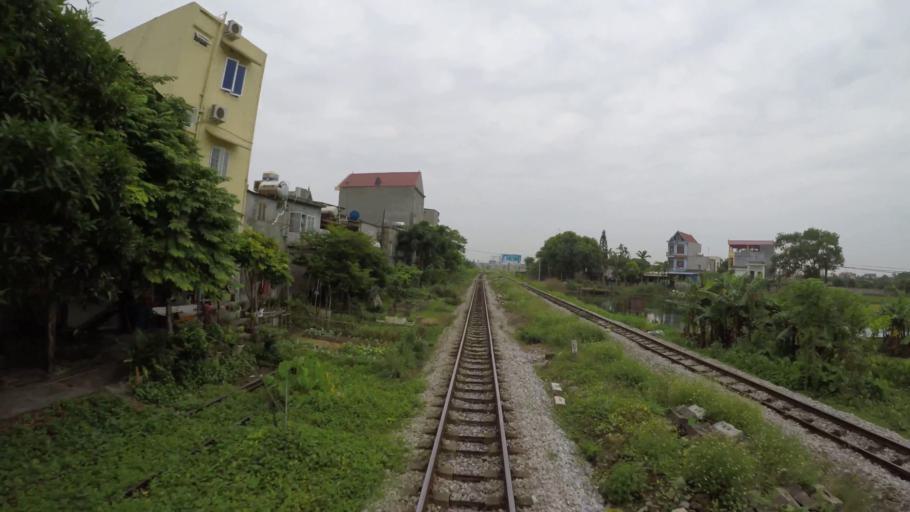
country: VN
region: Hai Duong
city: Phu Thai
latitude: 20.9326
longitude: 106.5524
